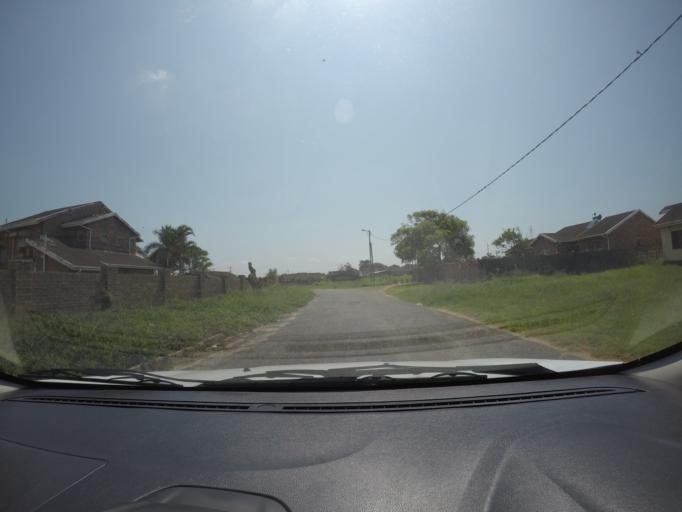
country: ZA
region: KwaZulu-Natal
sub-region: uThungulu District Municipality
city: eSikhawini
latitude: -28.8642
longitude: 31.9242
